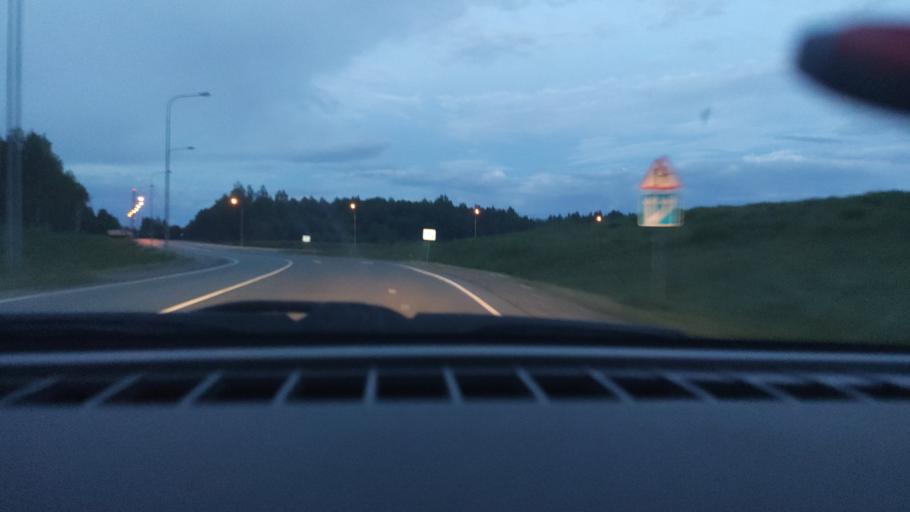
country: RU
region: Perm
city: Zvezdnyy
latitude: 57.7362
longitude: 56.3464
